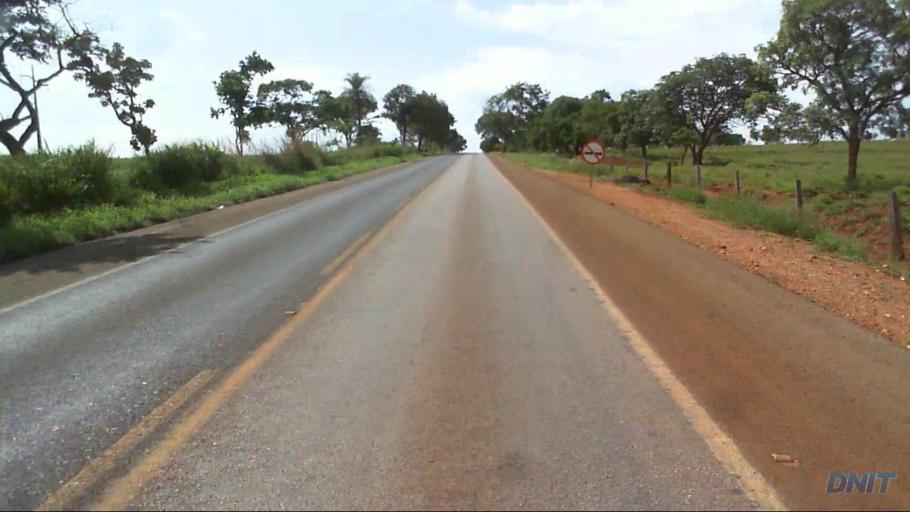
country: BR
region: Goias
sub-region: Barro Alto
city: Barro Alto
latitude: -15.0178
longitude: -48.8985
